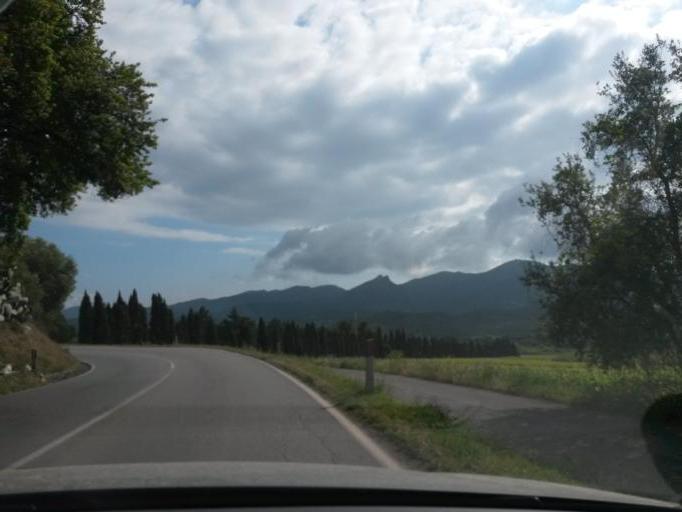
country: IT
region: Tuscany
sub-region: Provincia di Livorno
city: Portoferraio
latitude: 42.7861
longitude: 10.3401
